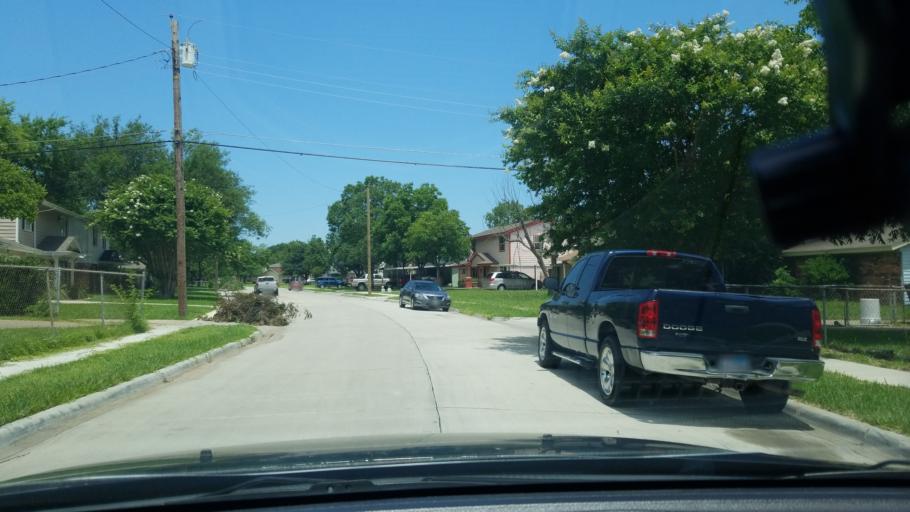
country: US
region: Texas
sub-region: Dallas County
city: Mesquite
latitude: 32.8052
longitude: -96.6543
